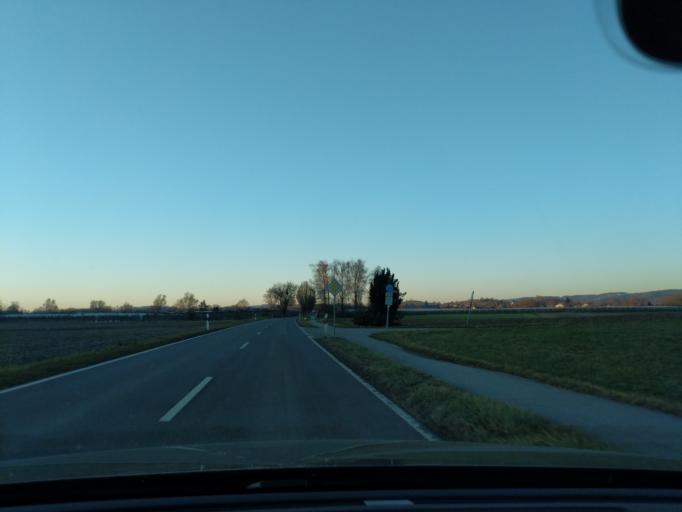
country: DE
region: Baden-Wuerttemberg
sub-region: Tuebingen Region
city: Bermatingen
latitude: 47.7167
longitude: 9.3312
